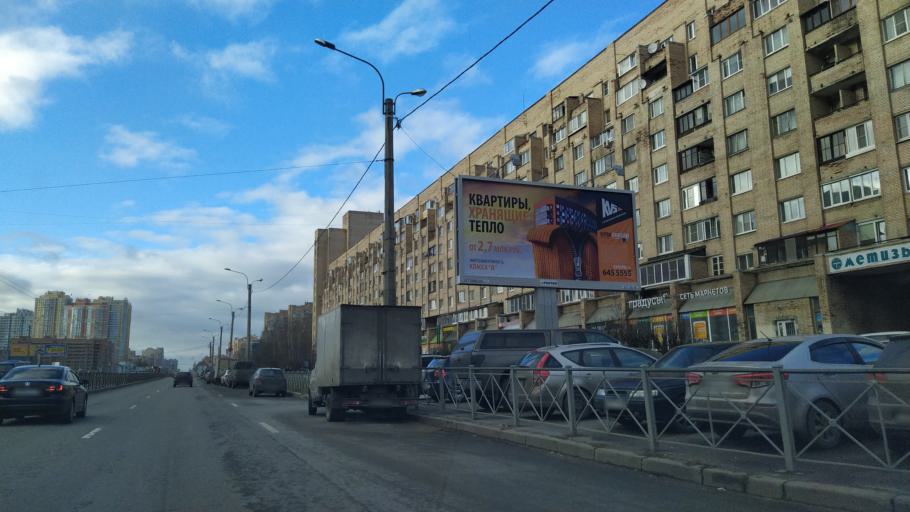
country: RU
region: St.-Petersburg
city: Grazhdanka
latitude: 60.0437
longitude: 30.3805
